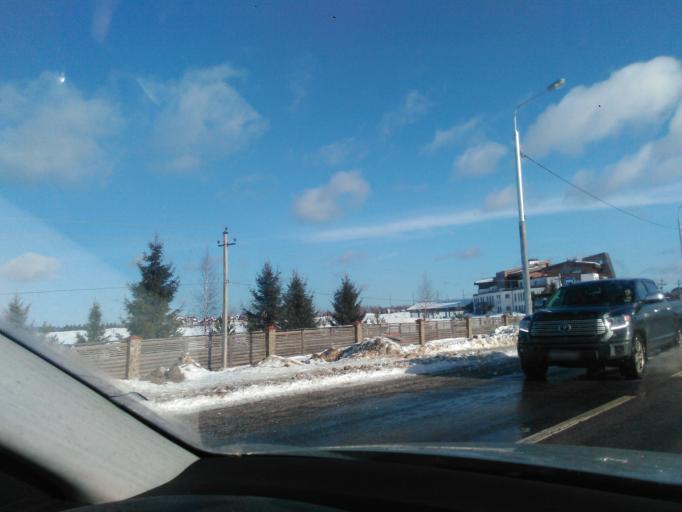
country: RU
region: Moskovskaya
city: Dedenevo
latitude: 56.2778
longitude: 37.5516
